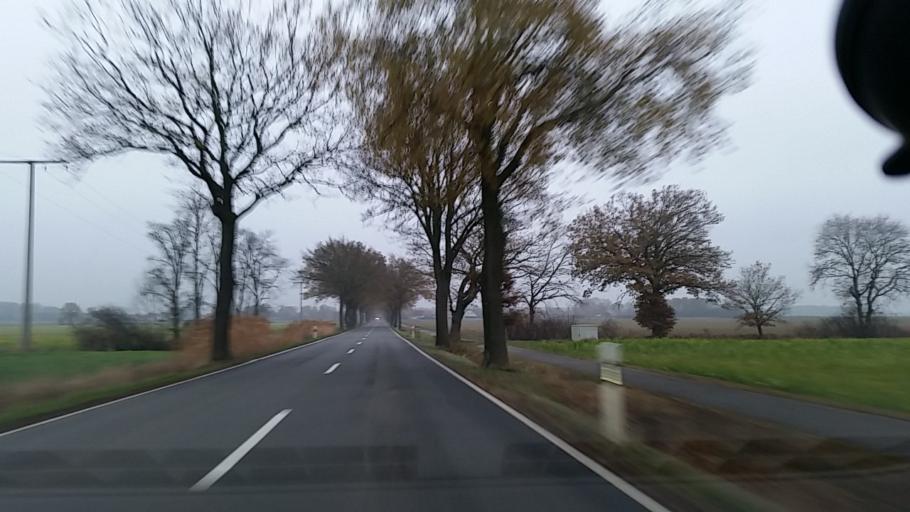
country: DE
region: Lower Saxony
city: Tiddische
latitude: 52.5096
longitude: 10.8039
